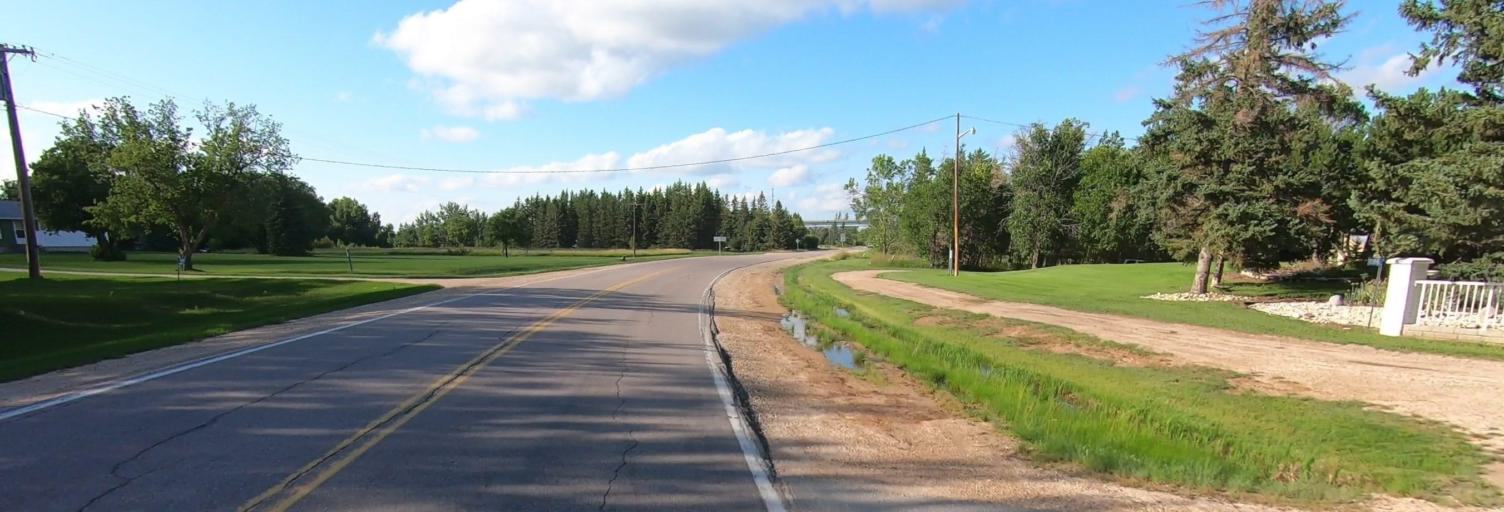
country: CA
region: Manitoba
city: Selkirk
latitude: 50.1868
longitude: -96.8456
